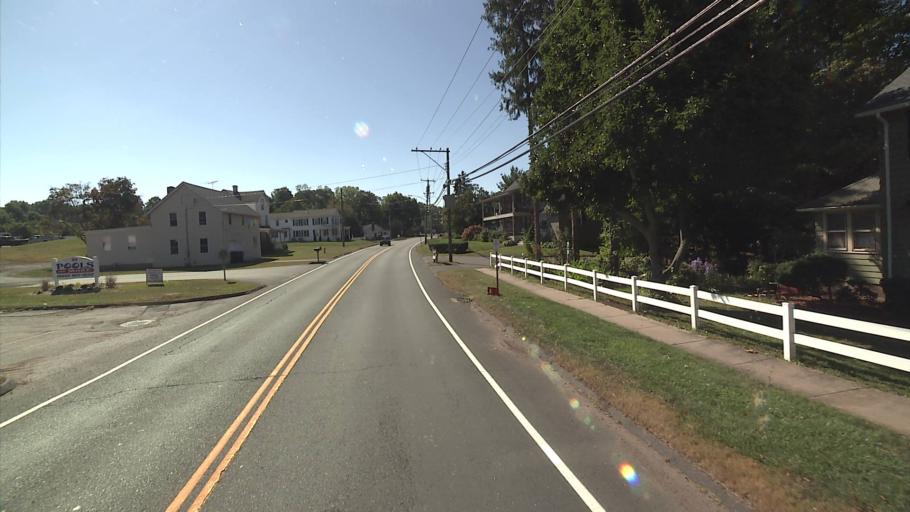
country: US
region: Connecticut
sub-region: Tolland County
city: Rockville
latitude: 41.8735
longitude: -72.4633
